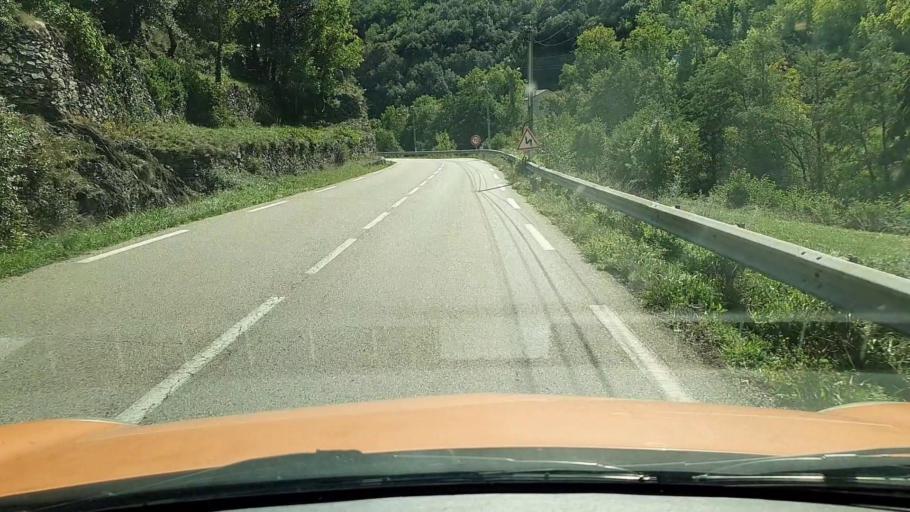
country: FR
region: Languedoc-Roussillon
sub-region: Departement du Gard
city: Valleraugue
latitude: 44.0832
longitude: 3.6199
